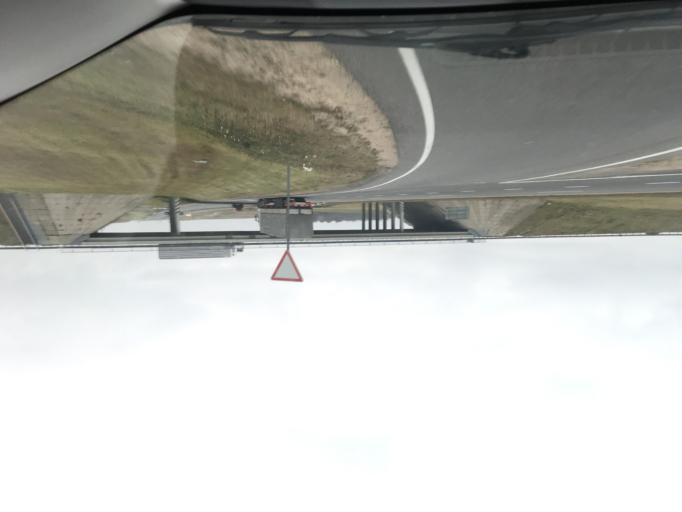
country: BY
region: Vitebsk
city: Vitebsk
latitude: 55.1548
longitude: 30.0638
